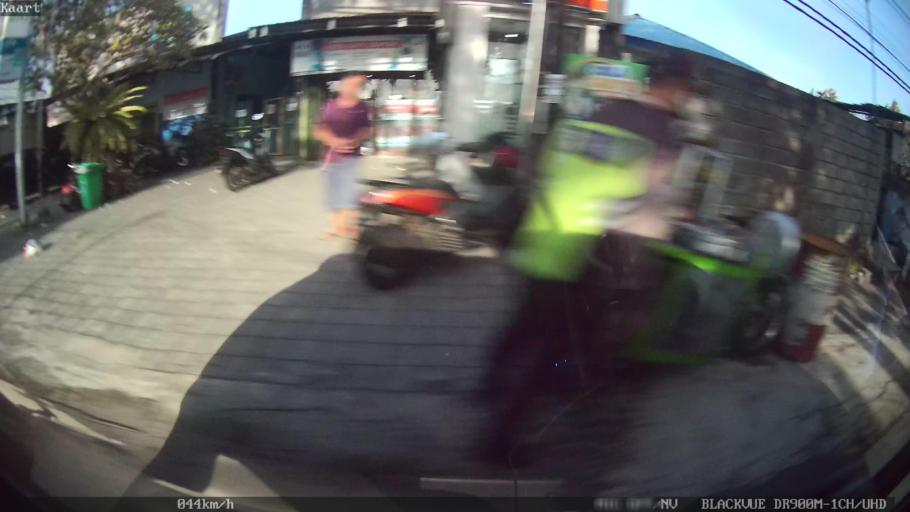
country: ID
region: Bali
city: Banjar Batur
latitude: -8.5978
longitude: 115.2147
